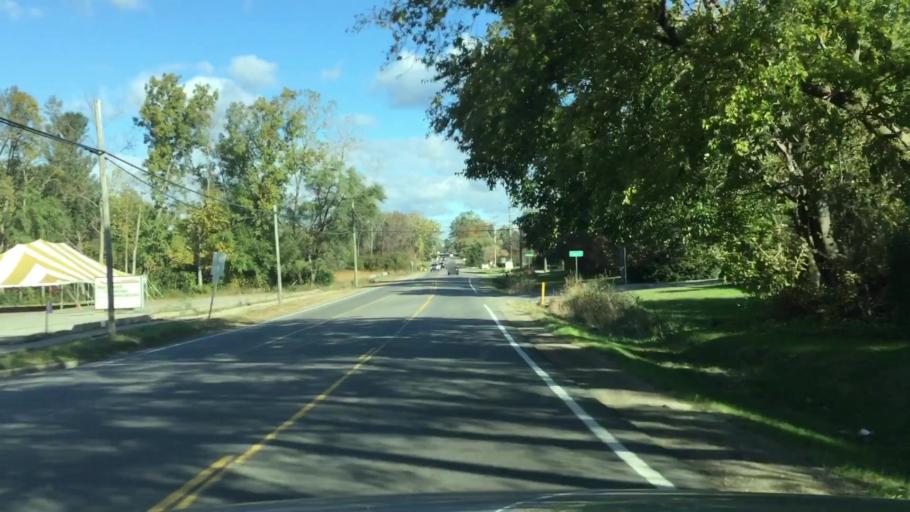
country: US
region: Michigan
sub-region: Oakland County
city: Waterford
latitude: 42.6621
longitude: -83.3863
